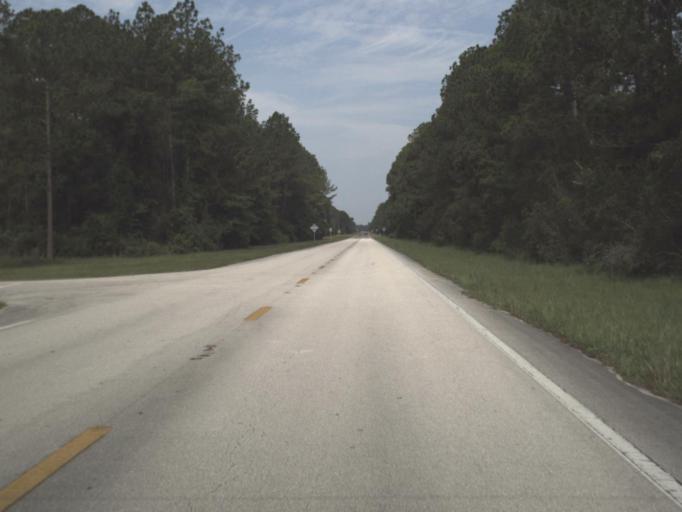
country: US
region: Florida
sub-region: Bradford County
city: Starke
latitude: 29.9385
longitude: -82.0445
